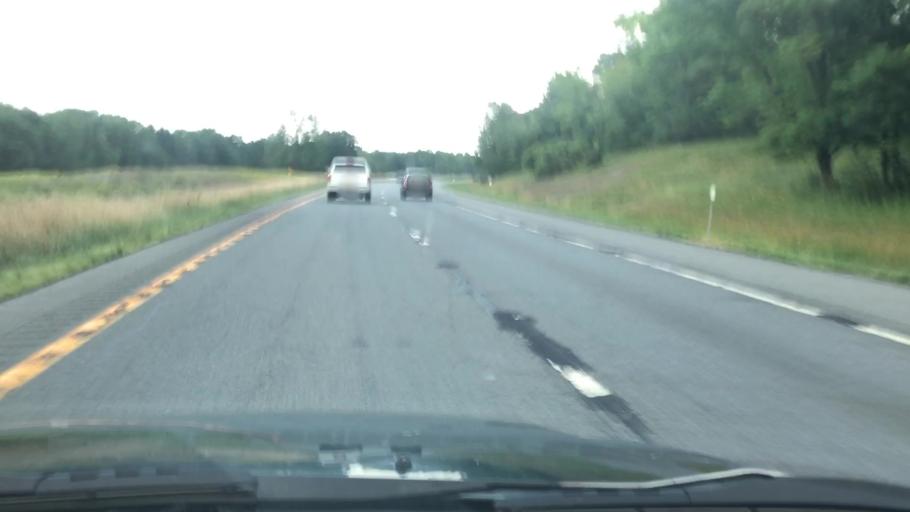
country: US
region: New York
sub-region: Orange County
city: Otisville
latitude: 41.3963
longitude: -74.5466
